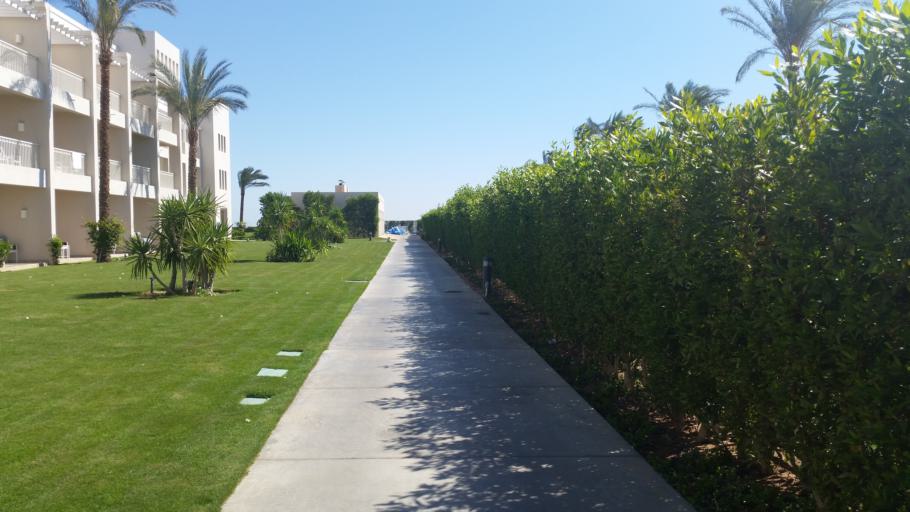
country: EG
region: Red Sea
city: Makadi Bay
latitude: 26.9822
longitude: 33.8753
